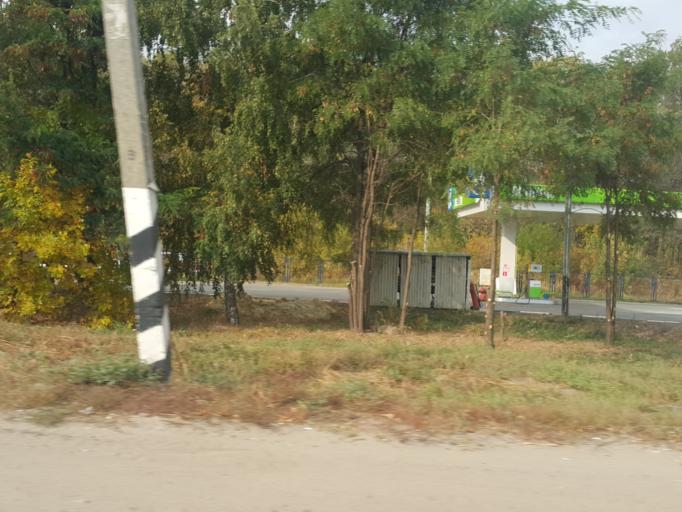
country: RU
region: Tambov
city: Bokino
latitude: 52.6564
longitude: 41.4465
